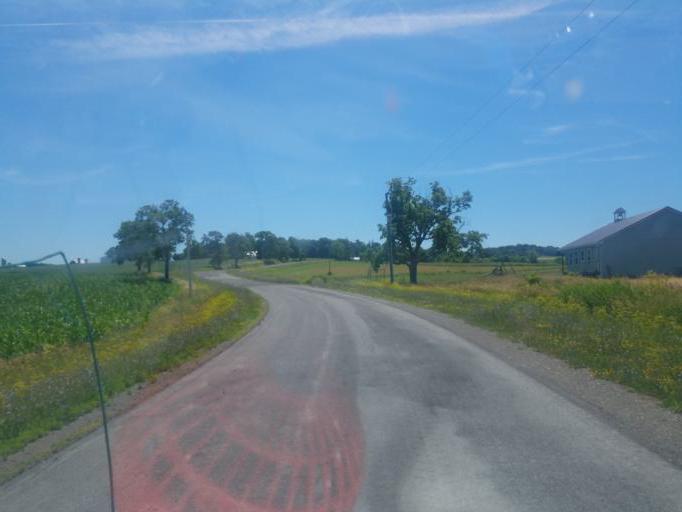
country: US
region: New York
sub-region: Yates County
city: Penn Yan
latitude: 42.6408
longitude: -77.0173
